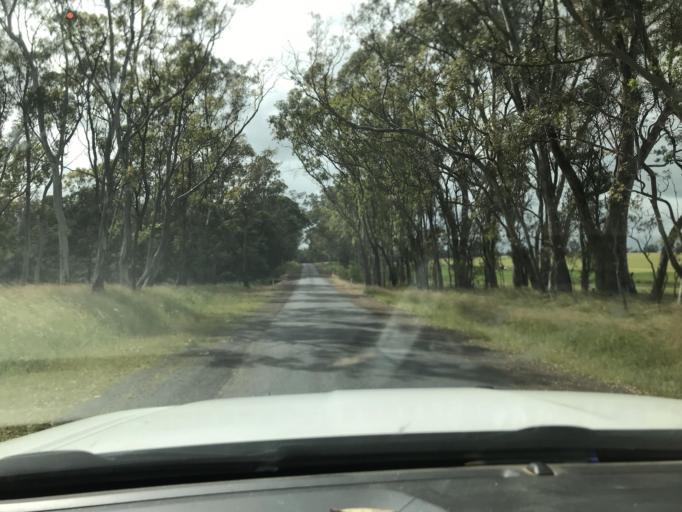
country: AU
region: South Australia
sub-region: Wattle Range
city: Penola
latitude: -37.1680
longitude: 141.4231
